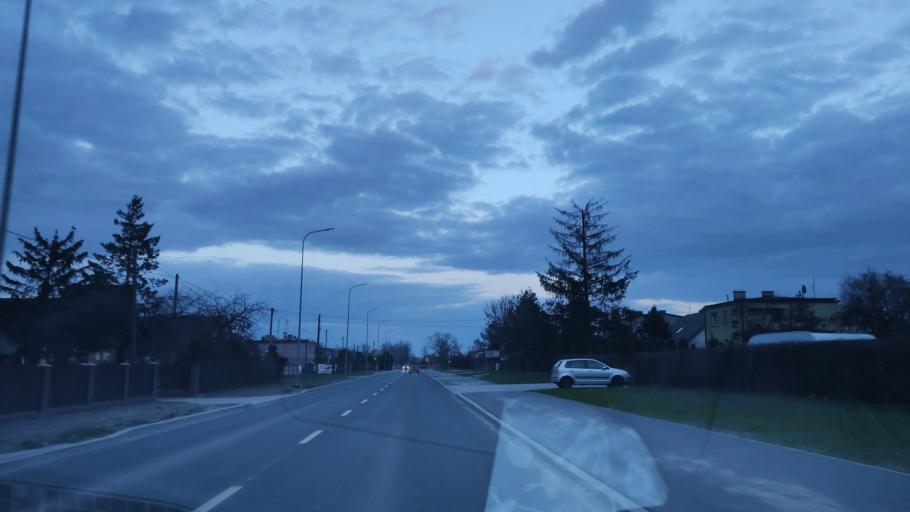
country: PL
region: Kujawsko-Pomorskie
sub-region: Powiat zninski
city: Znin
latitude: 52.8496
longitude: 17.7058
